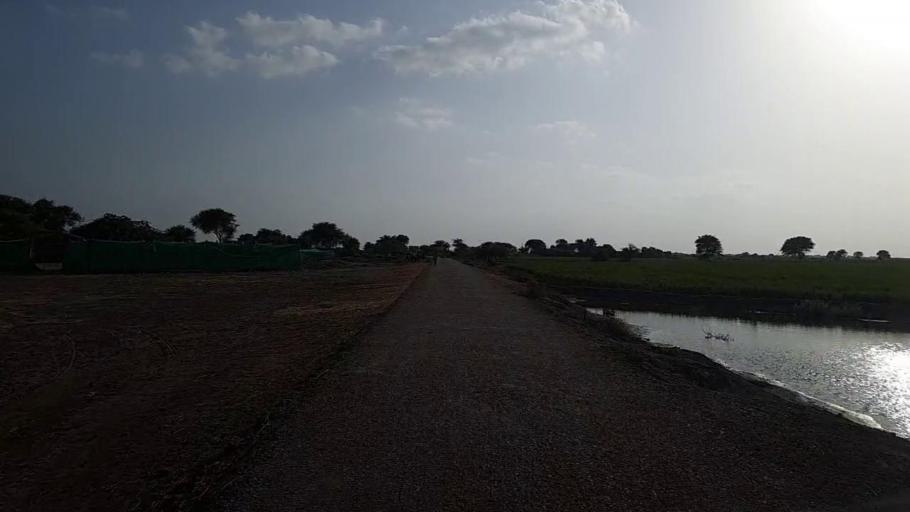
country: PK
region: Sindh
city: Kario
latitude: 24.6702
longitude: 68.4564
